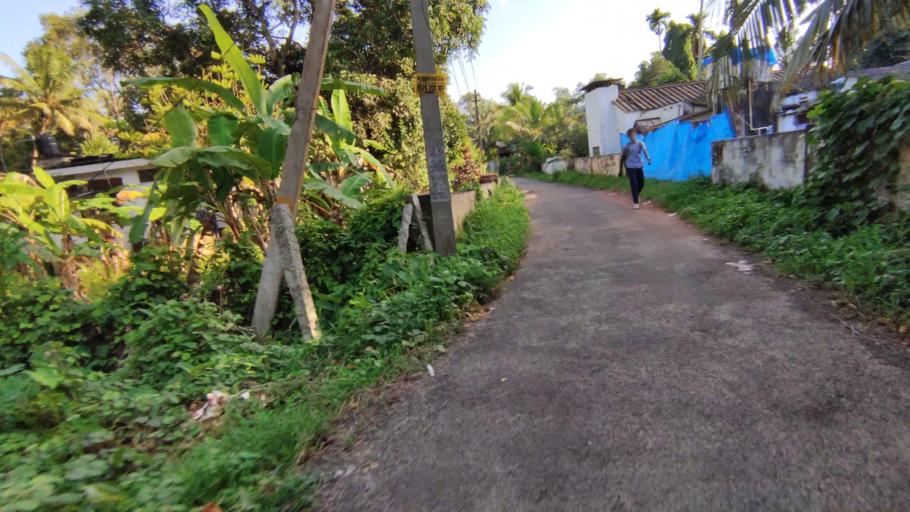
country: IN
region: Kerala
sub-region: Kottayam
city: Kottayam
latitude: 9.5949
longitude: 76.4838
